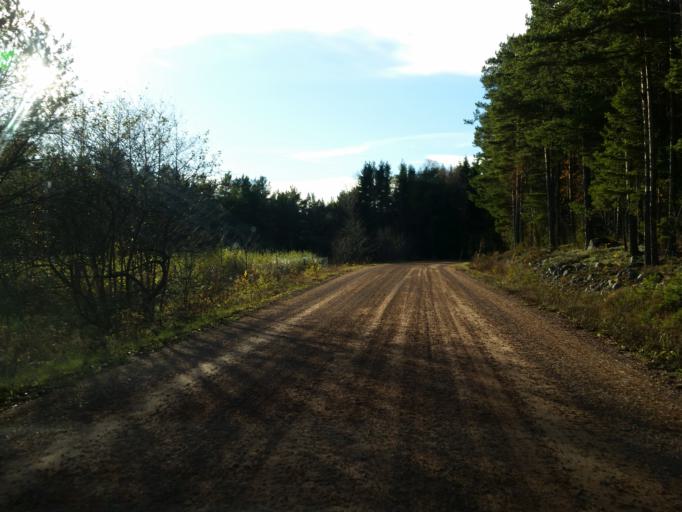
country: AX
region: Alands skaergard
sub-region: Kumlinge
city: Kumlinge
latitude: 60.2475
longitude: 20.7885
